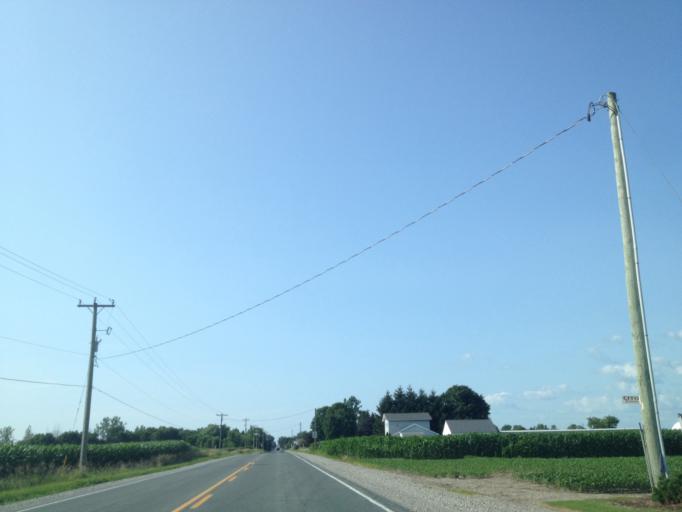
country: CA
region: Ontario
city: Aylmer
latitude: 42.8495
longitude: -80.8363
